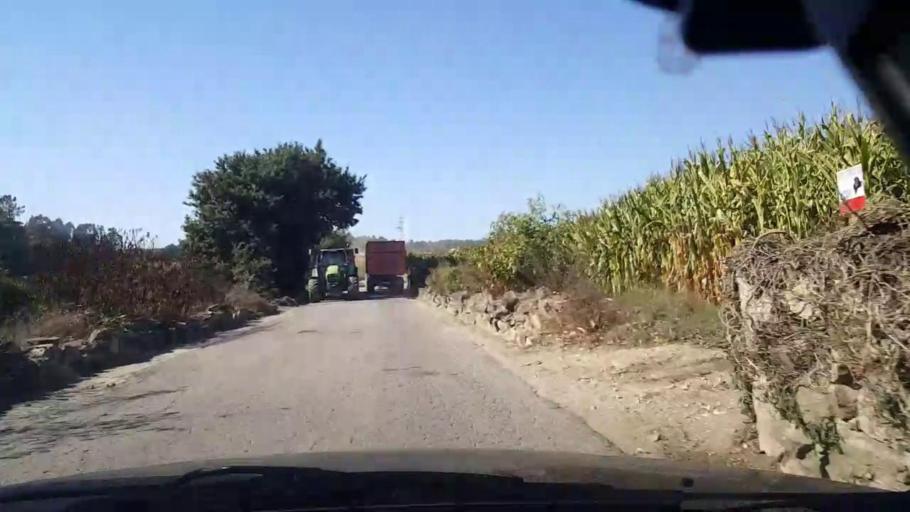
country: PT
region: Braga
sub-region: Vila Nova de Famalicao
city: Ribeirao
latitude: 41.3584
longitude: -8.6420
